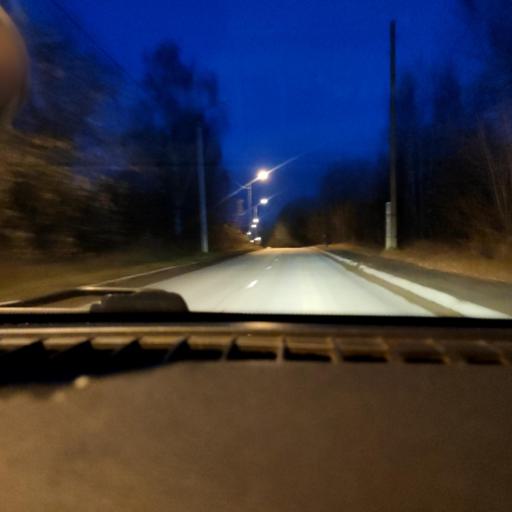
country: RU
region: Perm
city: Perm
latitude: 58.0268
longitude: 56.1748
